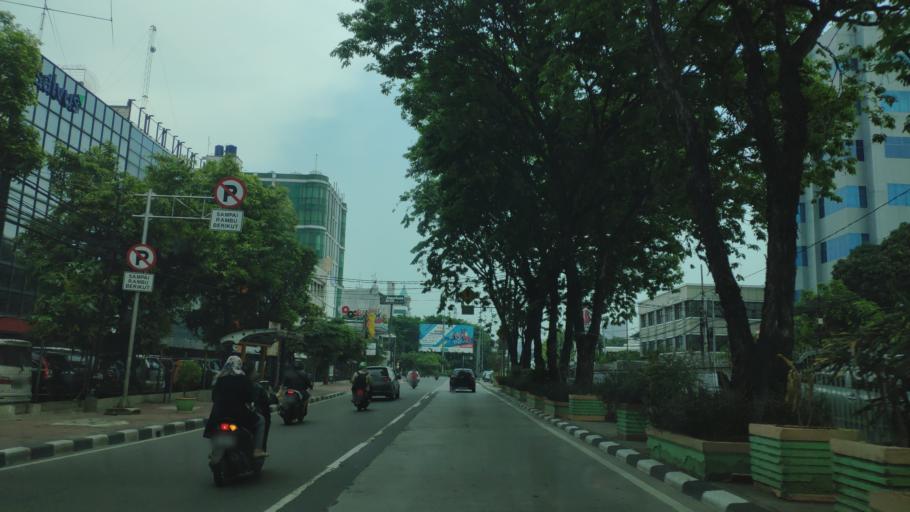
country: ID
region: Jakarta Raya
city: Jakarta
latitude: -6.1759
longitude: 106.8017
